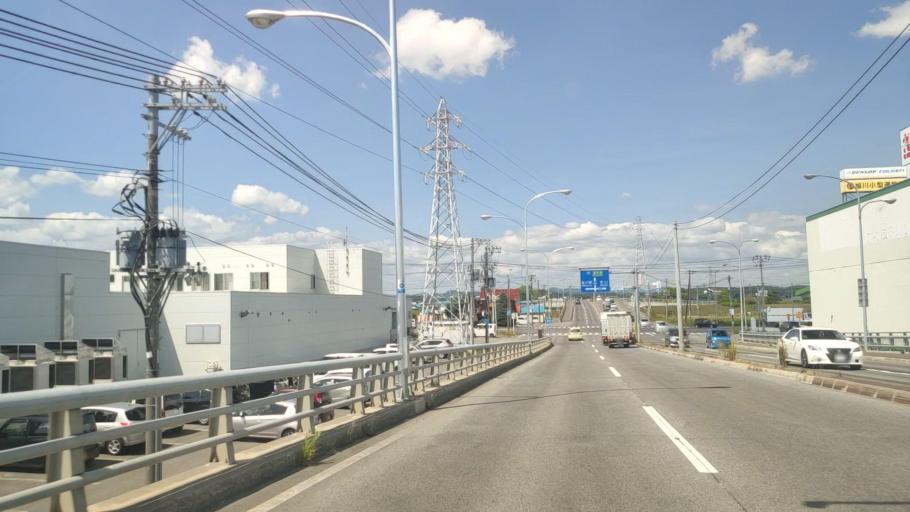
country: JP
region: Hokkaido
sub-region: Asahikawa-shi
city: Asahikawa
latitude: 43.7946
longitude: 142.3999
